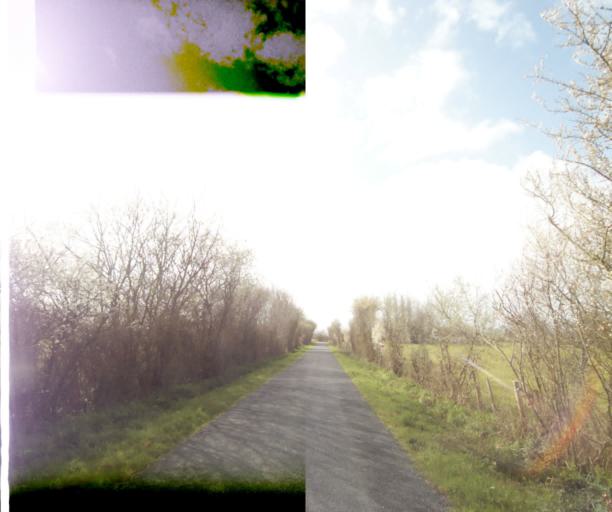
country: FR
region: Pays de la Loire
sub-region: Departement de la Loire-Atlantique
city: Bouvron
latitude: 47.4149
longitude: -1.8587
